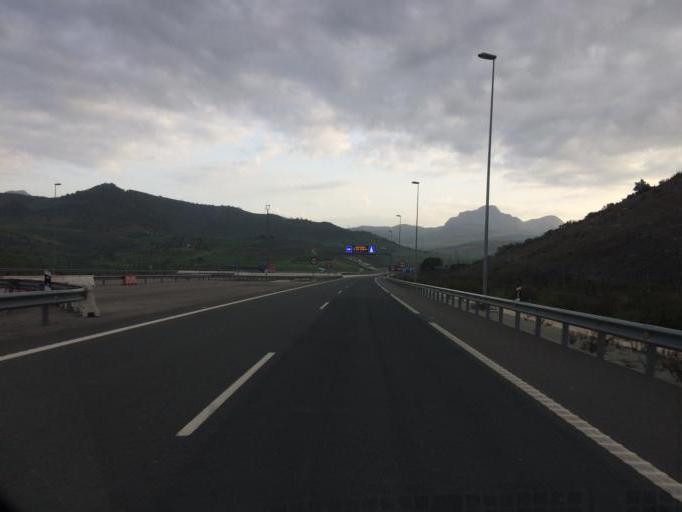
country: ES
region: Andalusia
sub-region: Provincia de Malaga
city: Casabermeja
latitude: 36.8963
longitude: -4.4639
